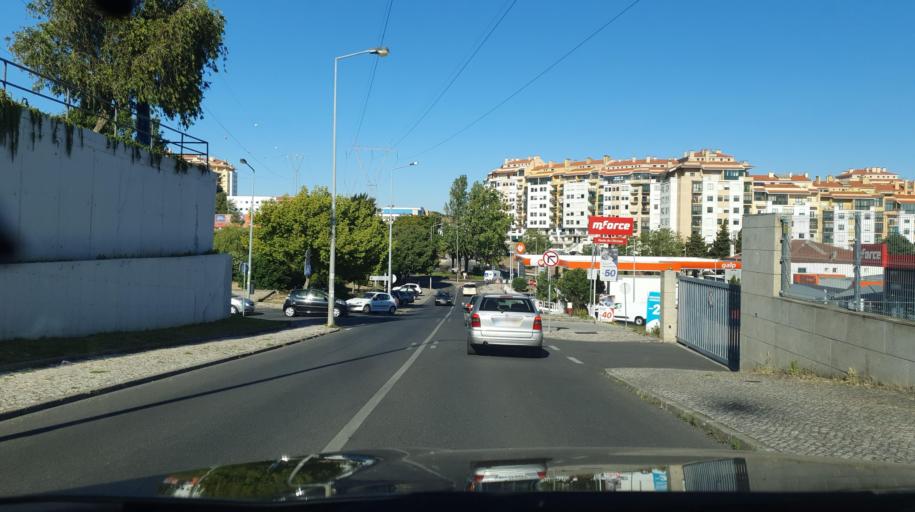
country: PT
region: Lisbon
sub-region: Sintra
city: Cacem
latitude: 38.7614
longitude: -9.2803
